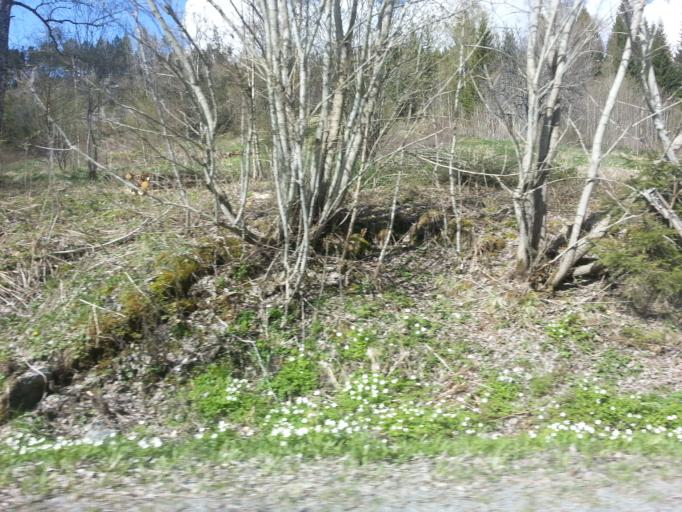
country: NO
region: Nord-Trondelag
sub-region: Levanger
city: Skogn
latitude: 63.6373
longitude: 11.2376
